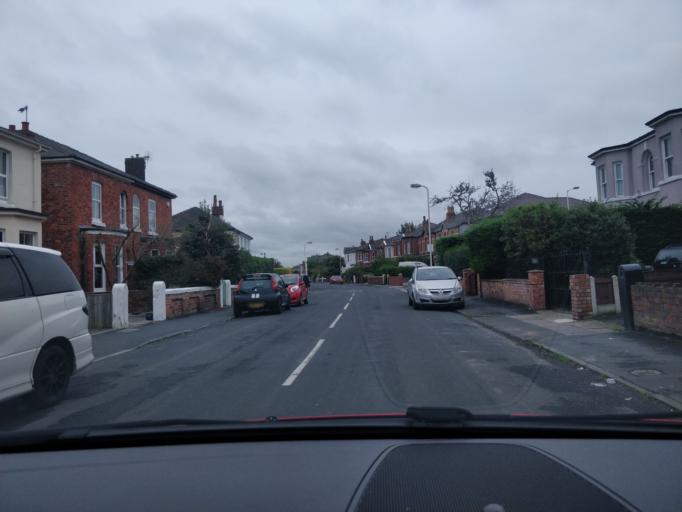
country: GB
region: England
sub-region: Sefton
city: Southport
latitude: 53.6402
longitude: -2.9987
